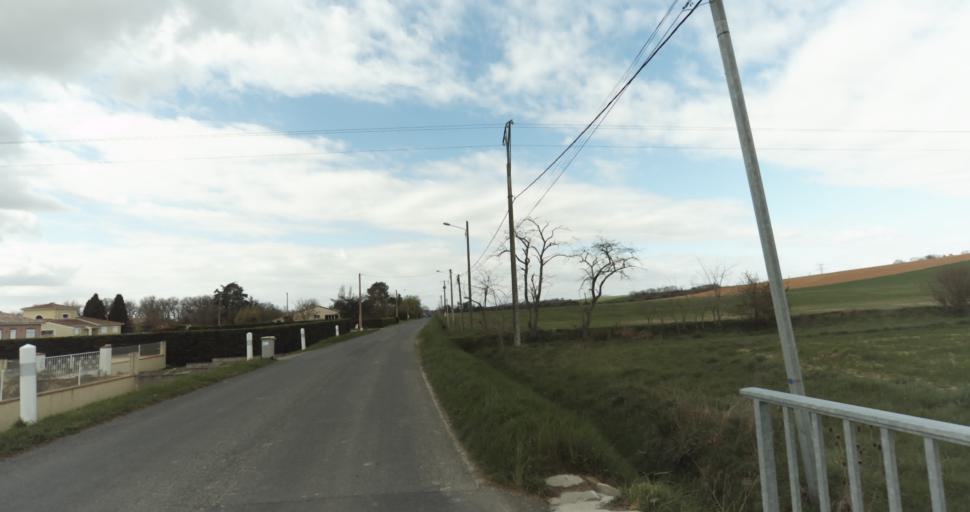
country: FR
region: Midi-Pyrenees
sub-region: Departement de la Haute-Garonne
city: Auterive
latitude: 43.3764
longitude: 1.4637
